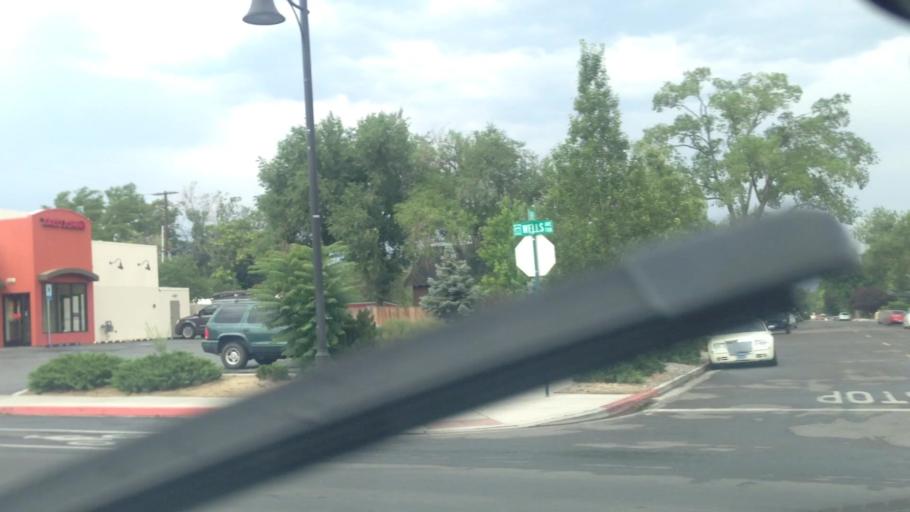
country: US
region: Nevada
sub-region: Washoe County
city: Reno
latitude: 39.5183
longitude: -119.8032
